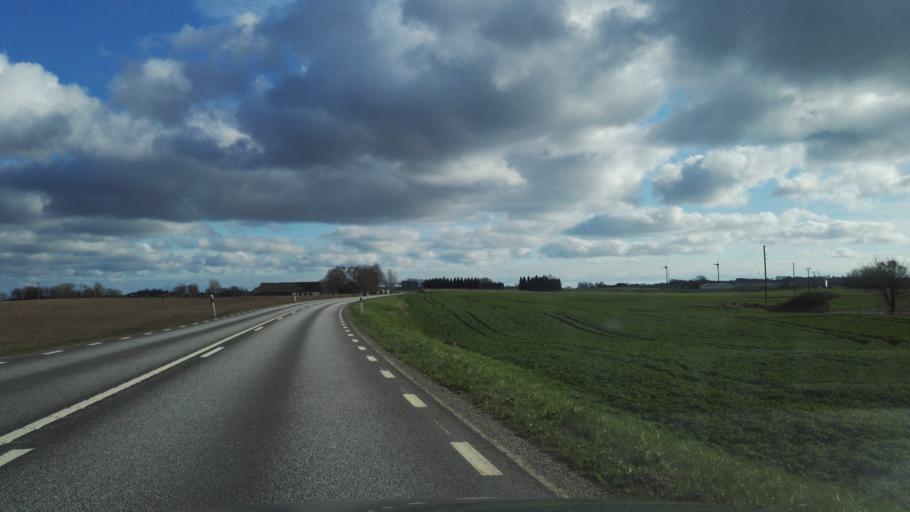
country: SE
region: Skane
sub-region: Ystads Kommun
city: Ystad
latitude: 55.4877
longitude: 13.8031
